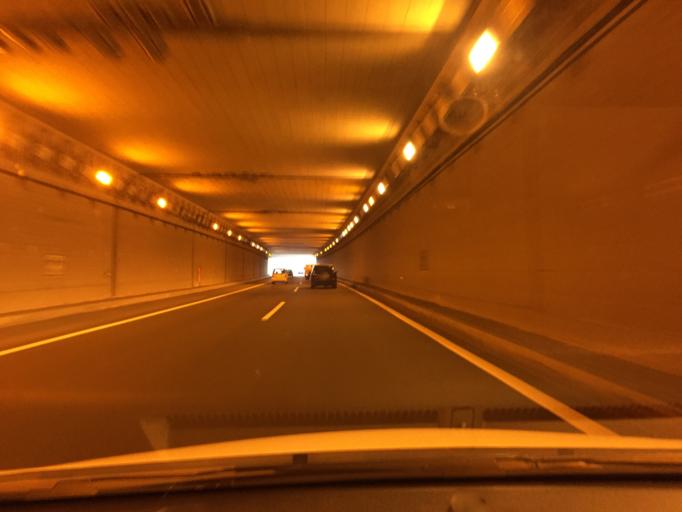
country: JP
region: Saitama
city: Hanno
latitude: 35.8064
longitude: 139.3419
